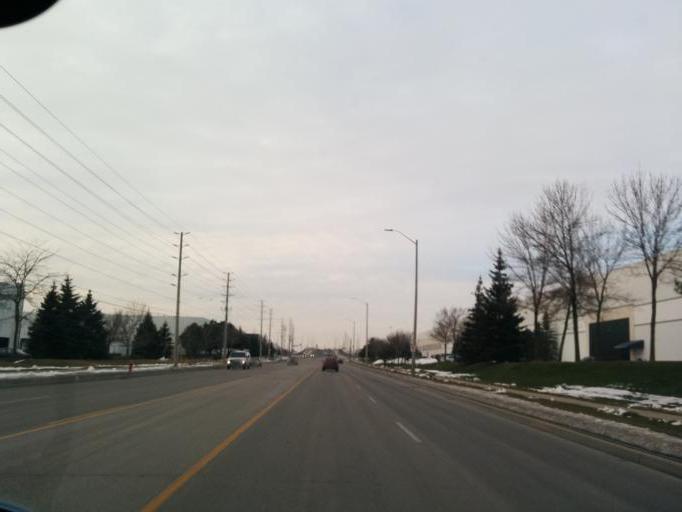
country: CA
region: Ontario
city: Mississauga
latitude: 43.6194
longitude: -79.6934
